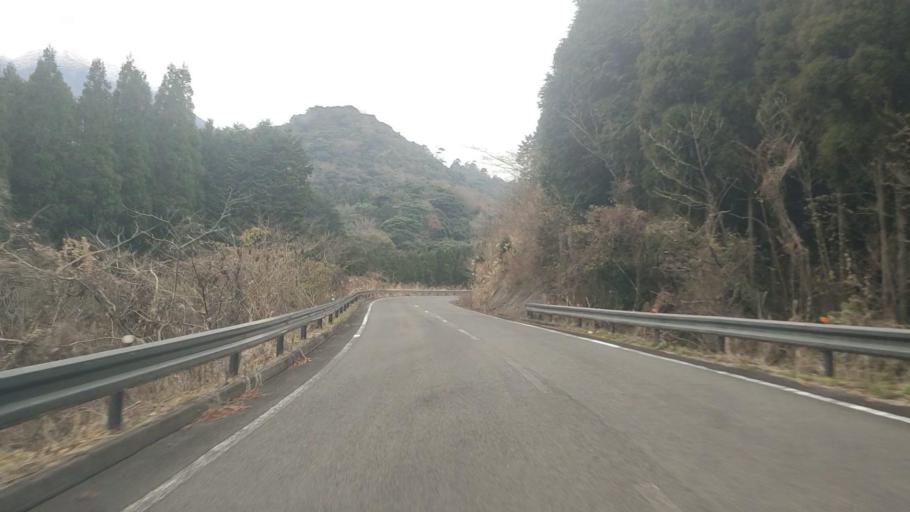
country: JP
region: Nagasaki
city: Shimabara
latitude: 32.7848
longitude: 130.2820
